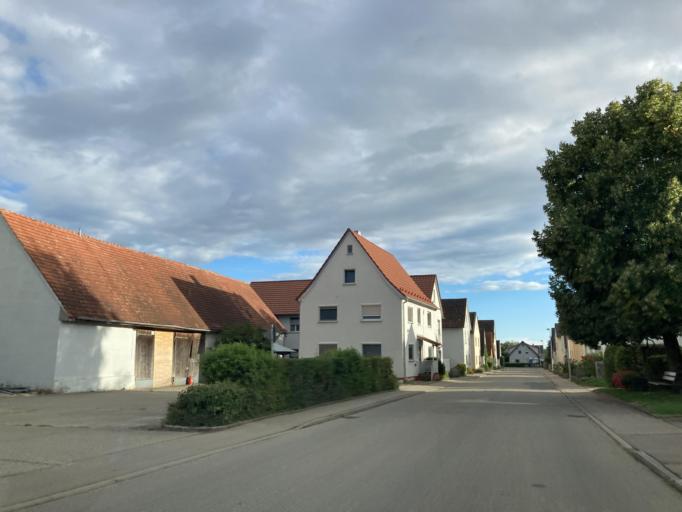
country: DE
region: Bavaria
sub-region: Swabia
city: Amerdingen
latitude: 48.7166
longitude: 10.4404
